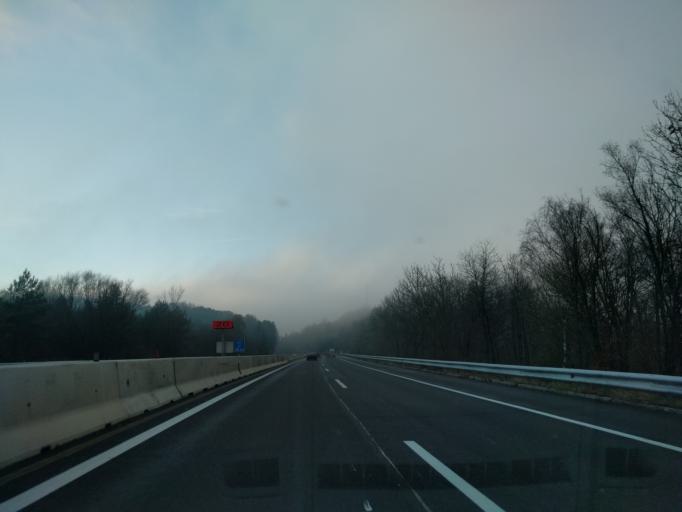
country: AT
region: Lower Austria
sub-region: Politischer Bezirk Wien-Umgebung
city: Pressbaum
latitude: 48.1769
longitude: 16.0972
